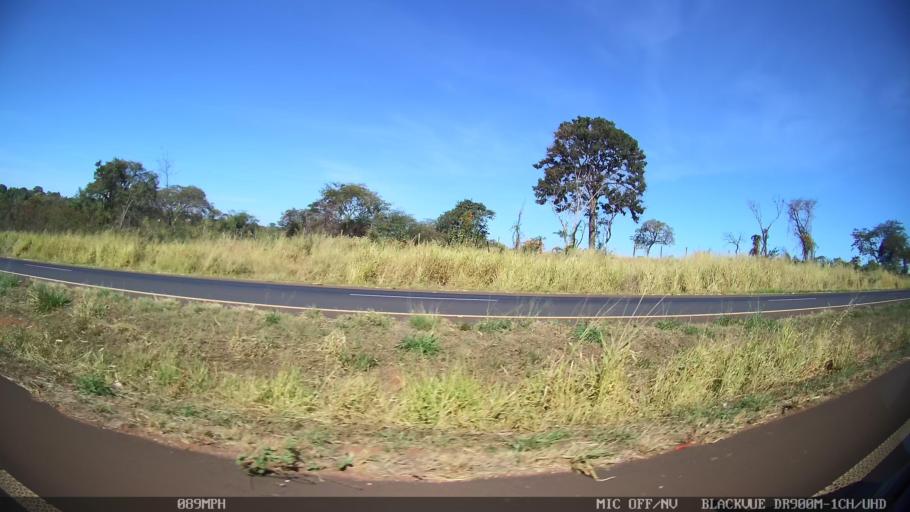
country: BR
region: Sao Paulo
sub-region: Barretos
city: Barretos
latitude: -20.5244
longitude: -48.5849
